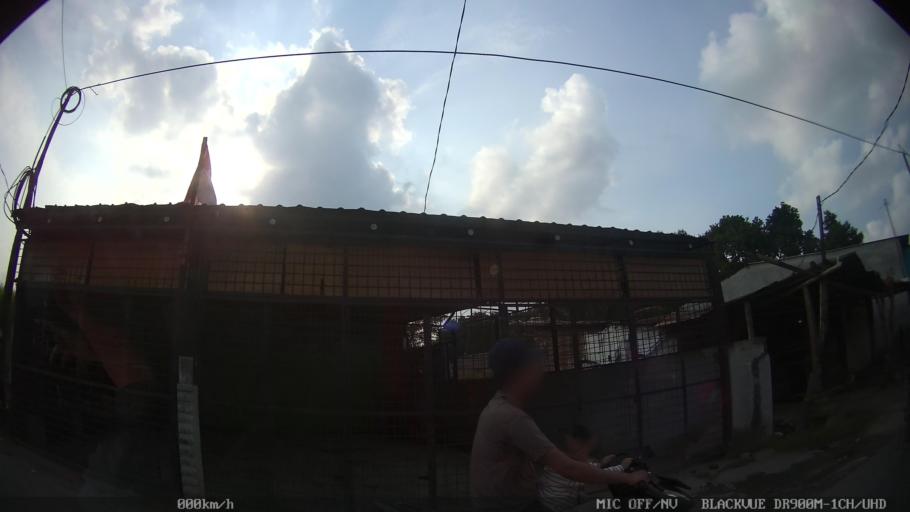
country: ID
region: North Sumatra
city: Medan
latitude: 3.5927
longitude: 98.7423
